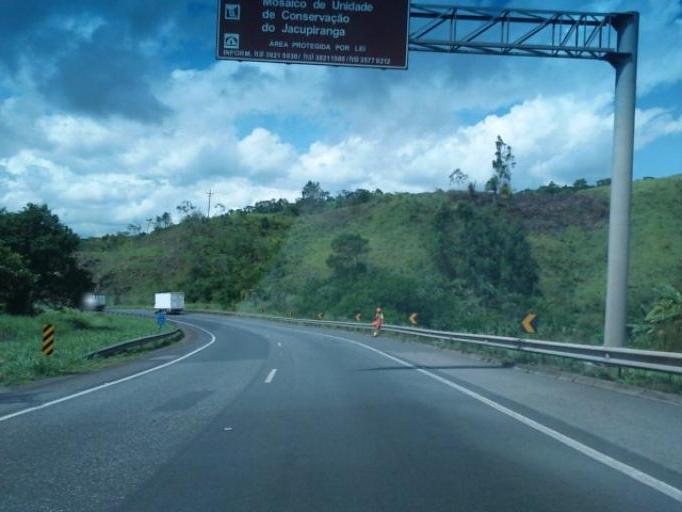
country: BR
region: Sao Paulo
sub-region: Cajati
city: Cajati
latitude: -24.8303
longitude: -48.2093
